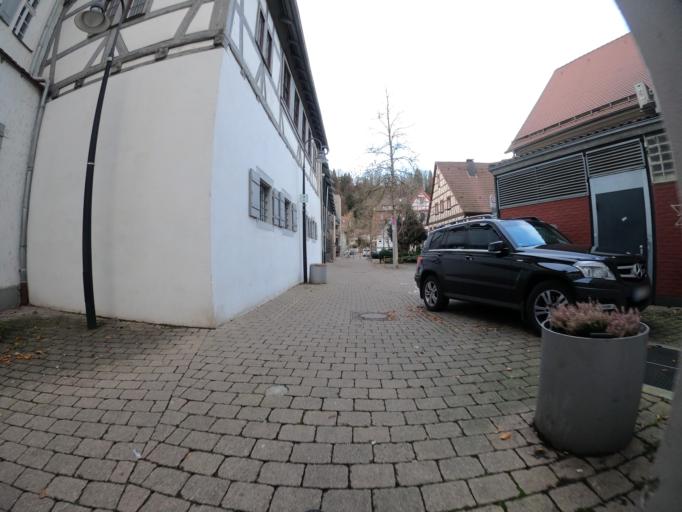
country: DE
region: Baden-Wuerttemberg
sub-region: Regierungsbezirk Stuttgart
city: Schwabisch Gmund
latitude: 48.8017
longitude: 9.7970
